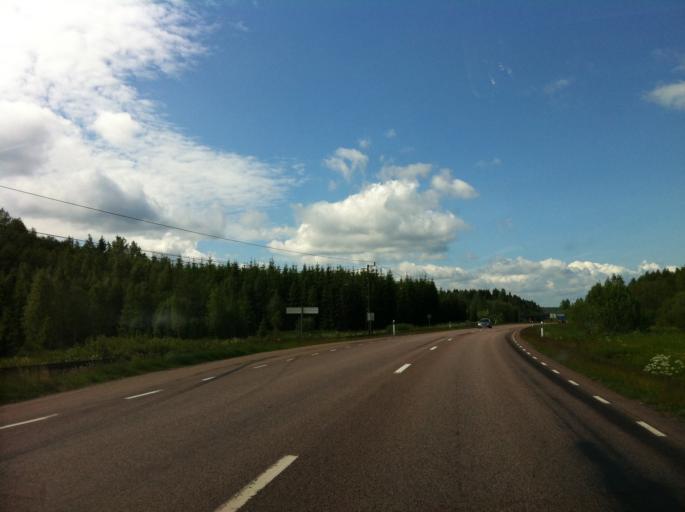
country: SE
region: Vaermland
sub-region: Karlstads Kommun
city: Valberg
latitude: 59.3744
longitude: 13.1508
